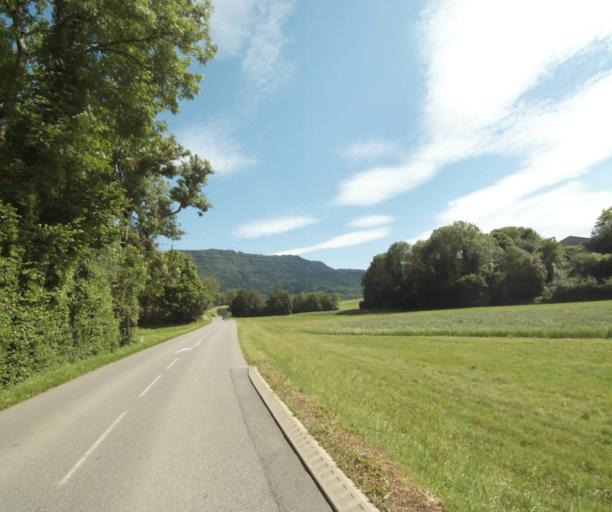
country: FR
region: Rhone-Alpes
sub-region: Departement de la Haute-Savoie
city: Perrignier
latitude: 46.3021
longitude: 6.4481
